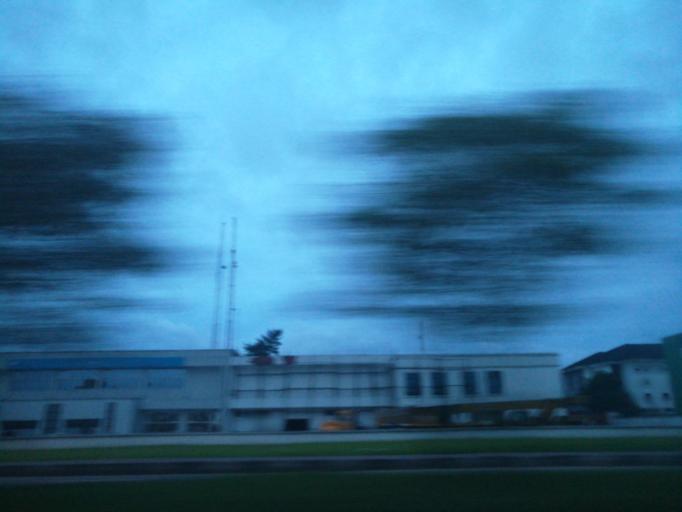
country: NG
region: Rivers
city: Port Harcourt
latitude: 4.7791
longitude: 7.0075
